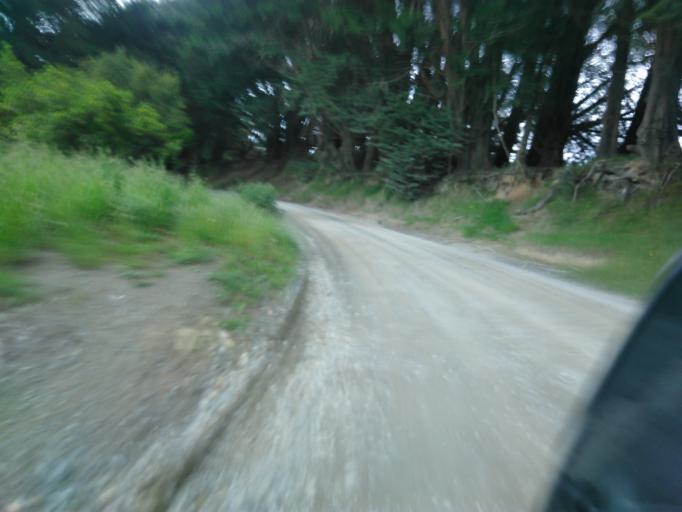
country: NZ
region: Gisborne
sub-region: Gisborne District
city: Gisborne
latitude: -38.0464
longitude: 178.0612
